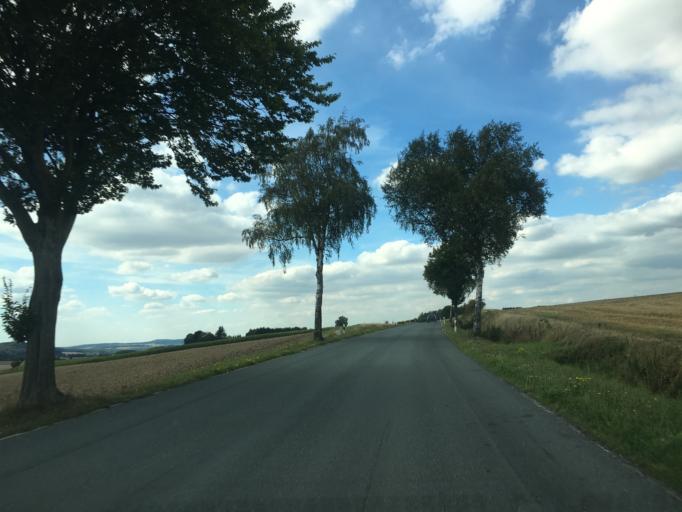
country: DE
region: North Rhine-Westphalia
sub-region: Regierungsbezirk Detmold
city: Lugde
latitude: 51.9727
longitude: 9.1838
